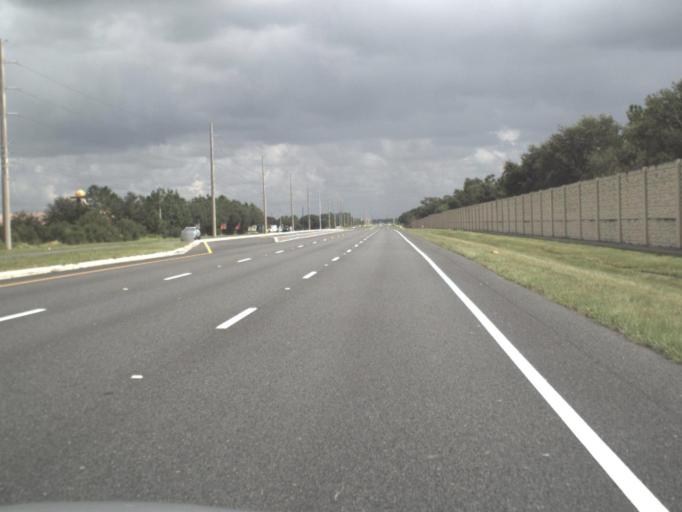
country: US
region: Florida
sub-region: Sarasota County
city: The Meadows
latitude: 27.4319
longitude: -82.4164
